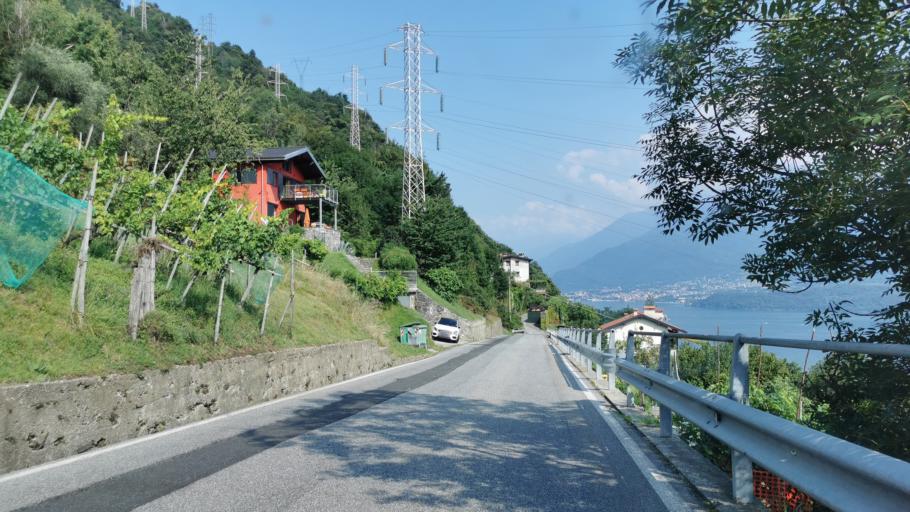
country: IT
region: Lombardy
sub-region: Provincia di Como
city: Gravedona-San Gregorio
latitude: 46.1523
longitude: 9.3008
